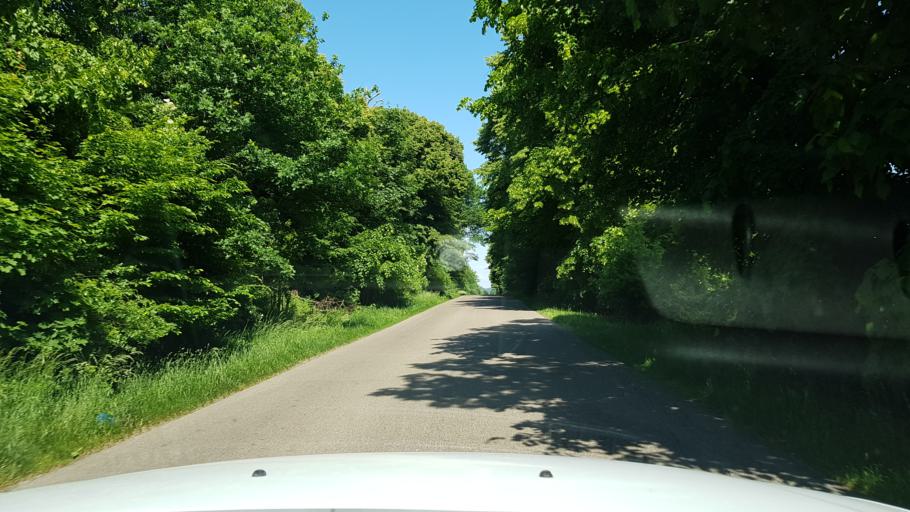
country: PL
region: West Pomeranian Voivodeship
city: Trzcinsko Zdroj
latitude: 53.0293
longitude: 14.5970
